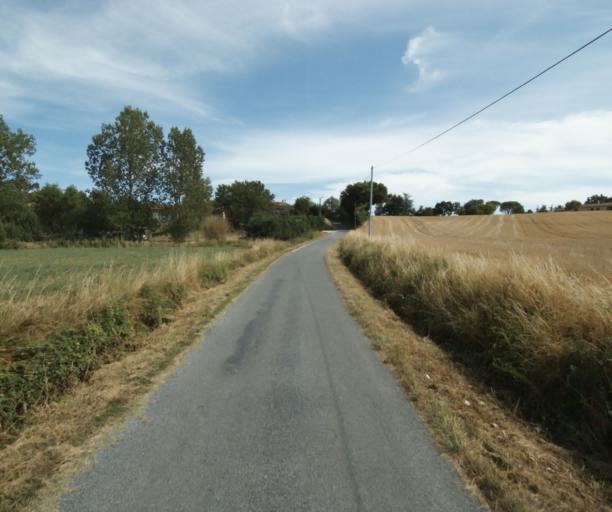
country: FR
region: Midi-Pyrenees
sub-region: Departement de la Haute-Garonne
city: Revel
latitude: 43.5133
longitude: 2.0318
